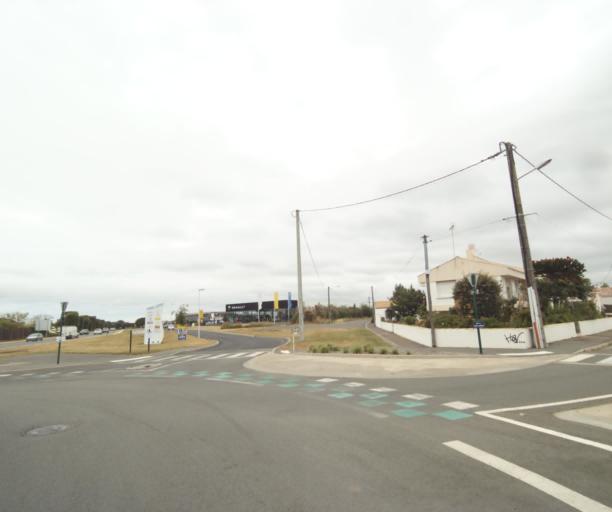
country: FR
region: Pays de la Loire
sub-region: Departement de la Vendee
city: Chateau-d'Olonne
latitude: 46.4954
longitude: -1.7520
